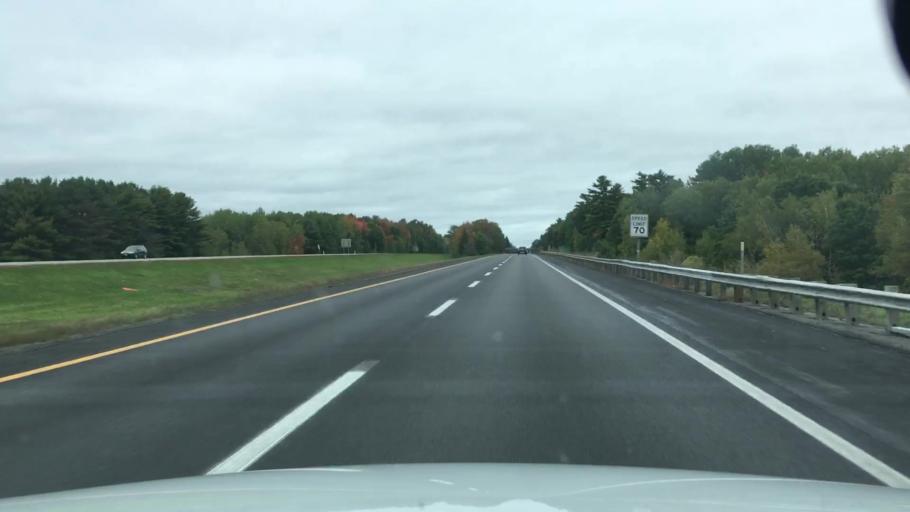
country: US
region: Maine
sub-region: Penobscot County
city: Veazie
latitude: 44.8386
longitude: -68.7362
